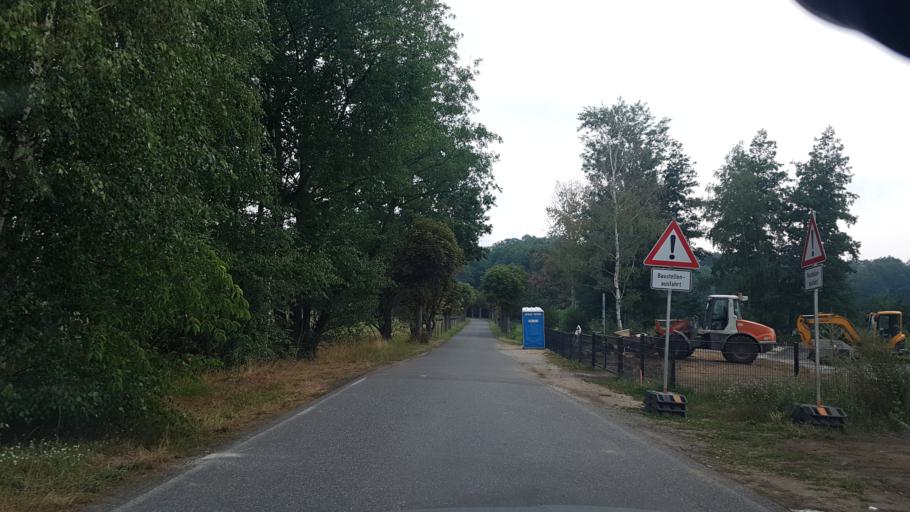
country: DE
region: Saxony
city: Bernsdorf
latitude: 51.3758
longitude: 14.0717
